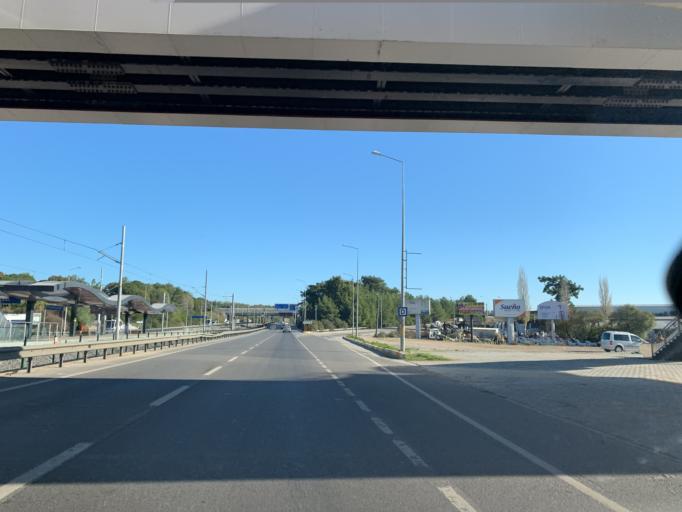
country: TR
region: Antalya
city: Aksu
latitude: 36.9429
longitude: 30.8275
